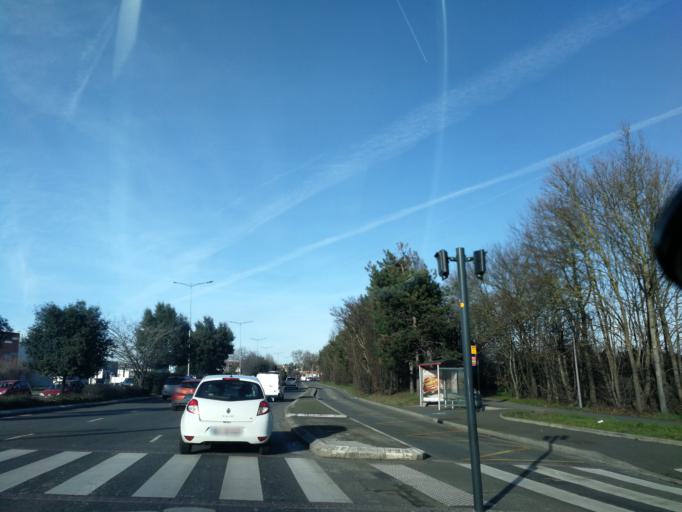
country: FR
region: Midi-Pyrenees
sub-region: Departement de la Haute-Garonne
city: L'Union
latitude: 43.6473
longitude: 1.4706
